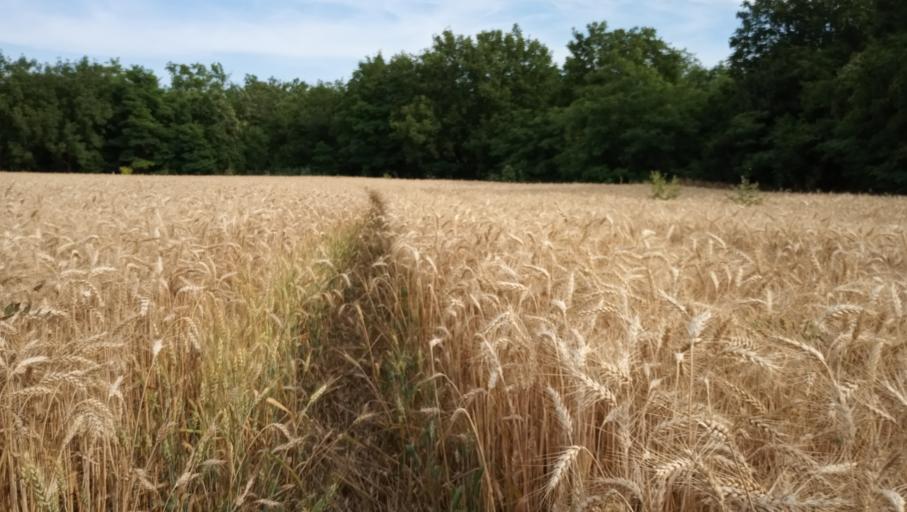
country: HU
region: Veszprem
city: Balatonkenese
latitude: 47.0406
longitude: 18.0814
